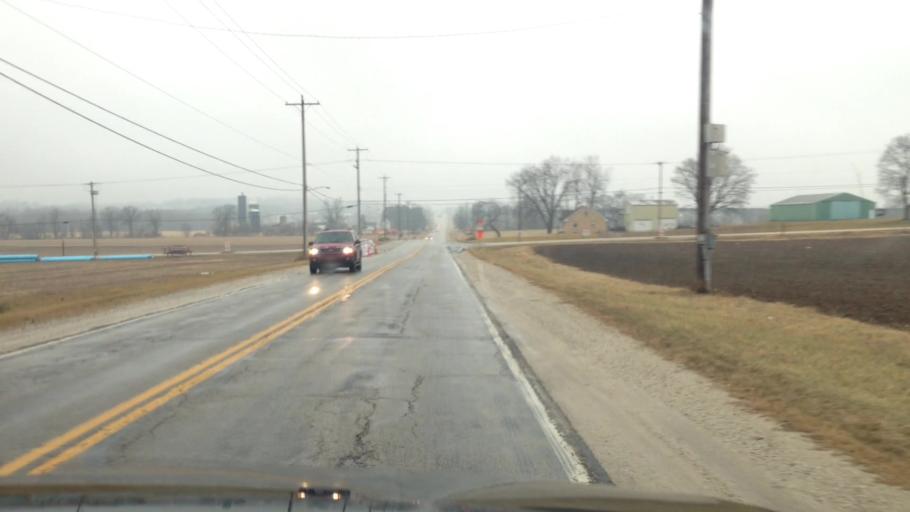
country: US
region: Wisconsin
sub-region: Washington County
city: Richfield
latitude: 43.2503
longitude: -88.1608
